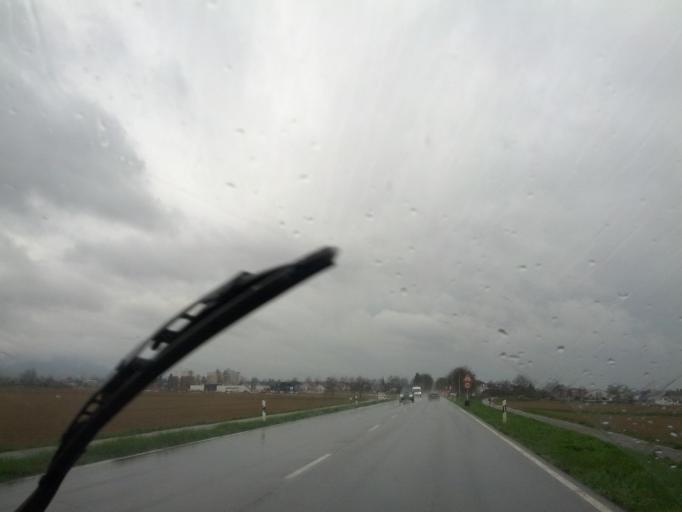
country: DE
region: Baden-Wuerttemberg
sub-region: Freiburg Region
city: Bad Krozingen
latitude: 47.9272
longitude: 7.7130
